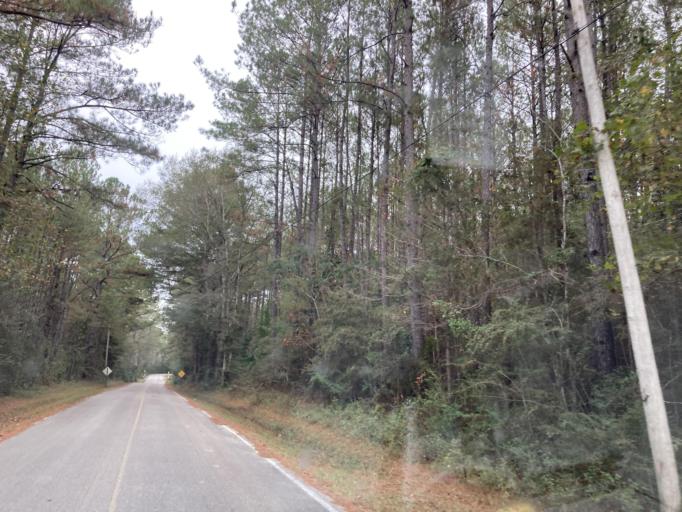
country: US
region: Mississippi
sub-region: Lamar County
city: Lumberton
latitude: 31.0671
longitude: -89.4329
